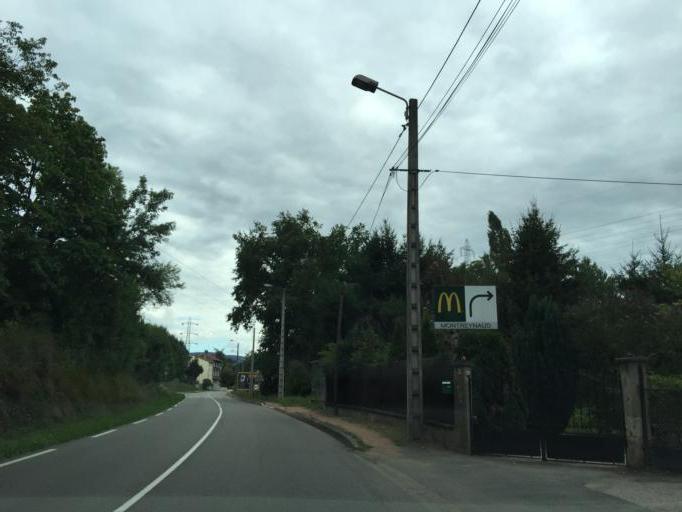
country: FR
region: Rhone-Alpes
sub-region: Departement de la Loire
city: La Talaudiere
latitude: 45.4690
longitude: 4.4118
